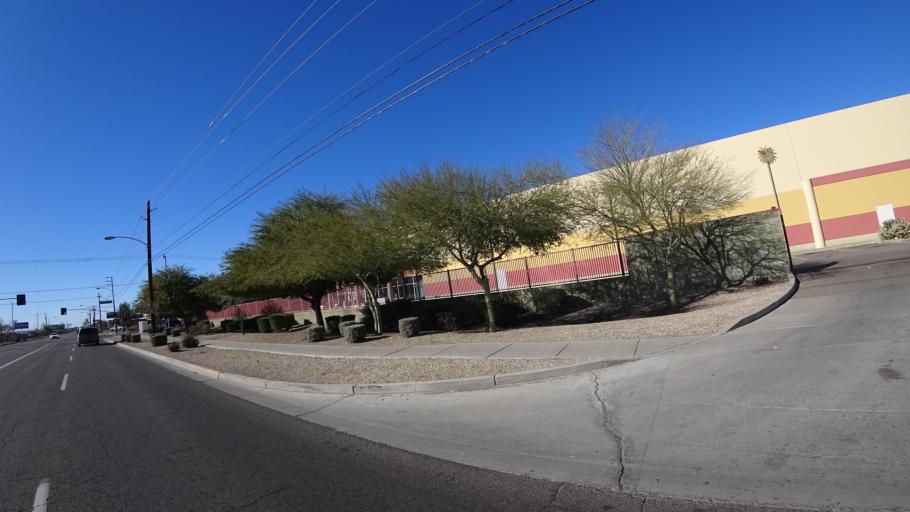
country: US
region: Arizona
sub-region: Maricopa County
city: Phoenix
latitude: 33.4368
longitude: -112.0990
